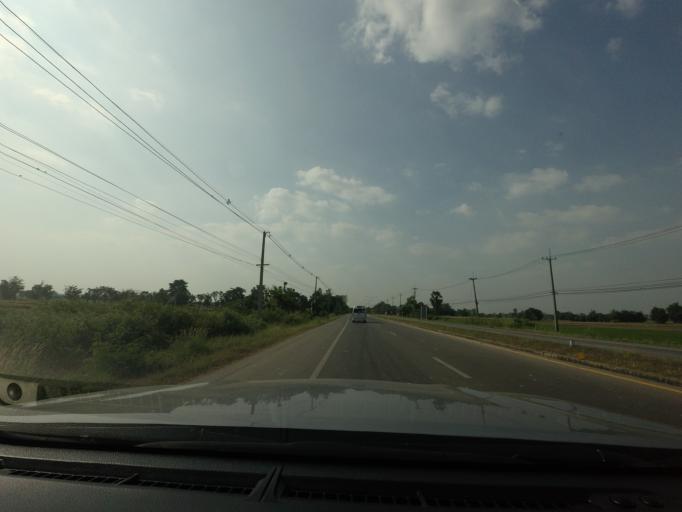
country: TH
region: Sukhothai
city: Kong Krailat
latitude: 17.0088
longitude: 99.9254
